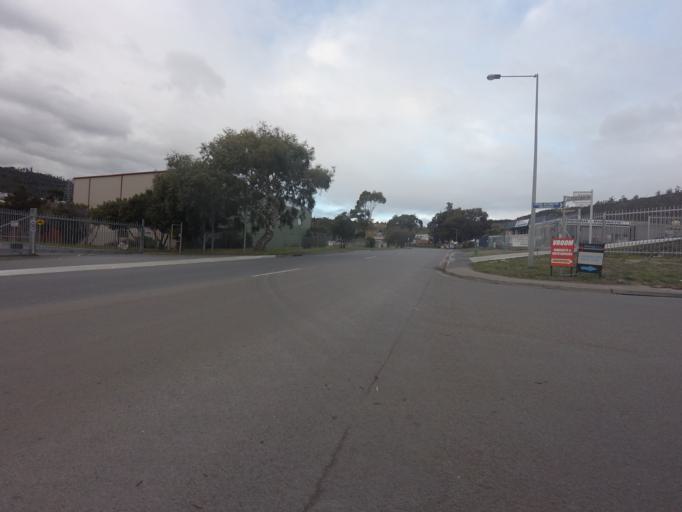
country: AU
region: Tasmania
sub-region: Clarence
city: Warrane
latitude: -42.8610
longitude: 147.4006
